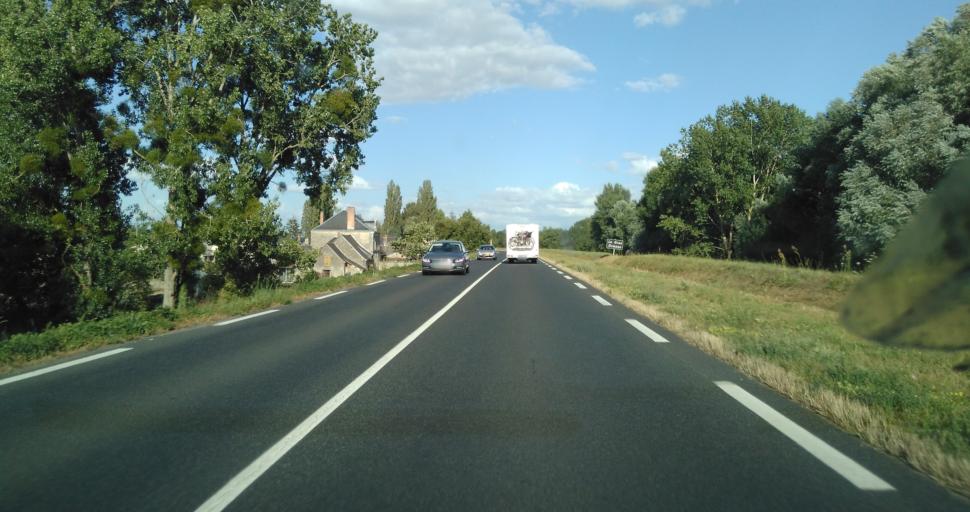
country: FR
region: Centre
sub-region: Departement d'Indre-et-Loire
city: Noizay
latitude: 47.4033
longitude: 0.8791
